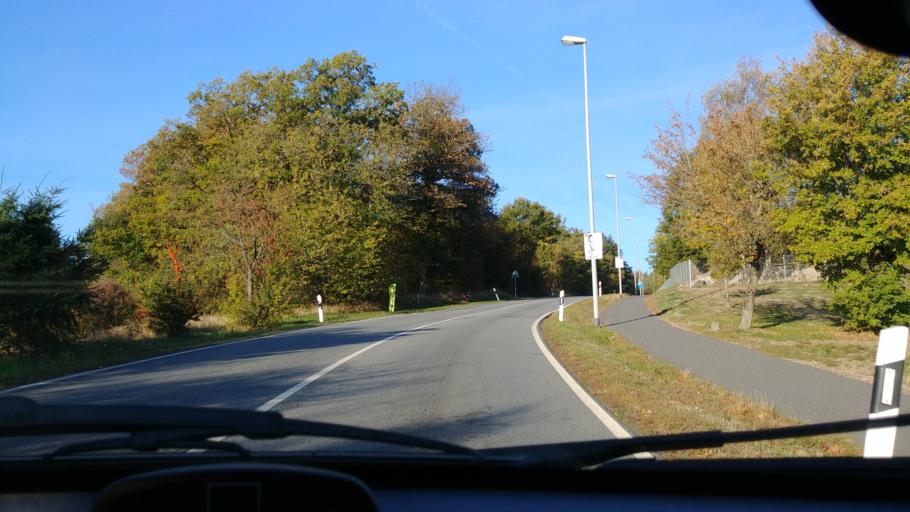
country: DE
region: Hesse
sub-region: Regierungsbezirk Darmstadt
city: Bad Schwalbach
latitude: 50.1408
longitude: 8.0561
